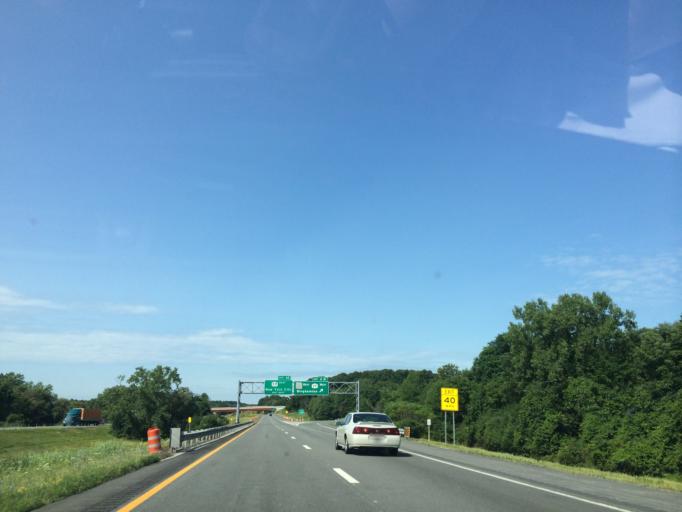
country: US
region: New York
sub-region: Orange County
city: Mechanicstown
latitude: 41.4514
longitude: -74.3628
